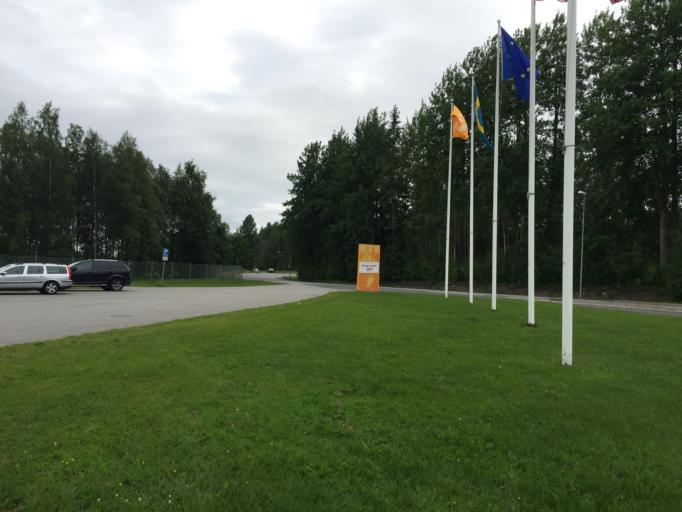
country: SE
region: Vaesterbotten
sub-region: Umea Kommun
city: Ersmark
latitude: 63.8431
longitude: 20.3407
